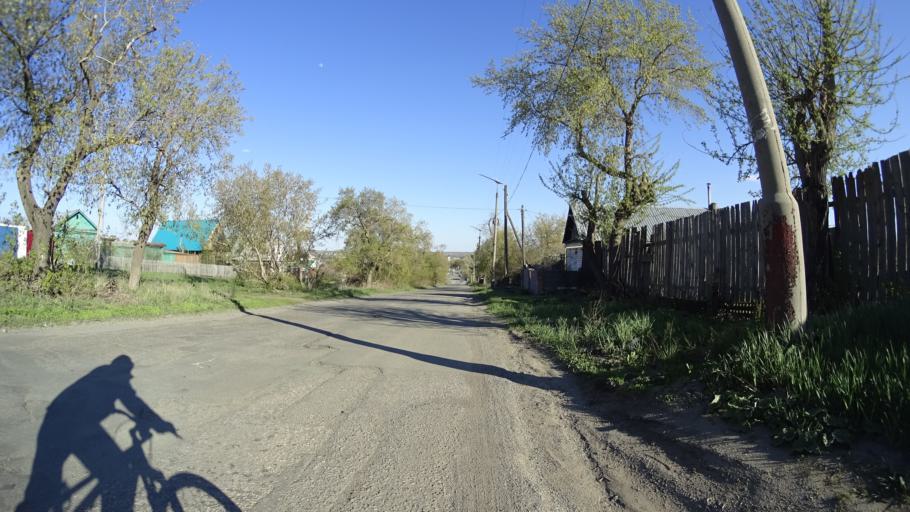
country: RU
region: Chelyabinsk
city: Troitsk
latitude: 54.0989
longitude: 61.5588
